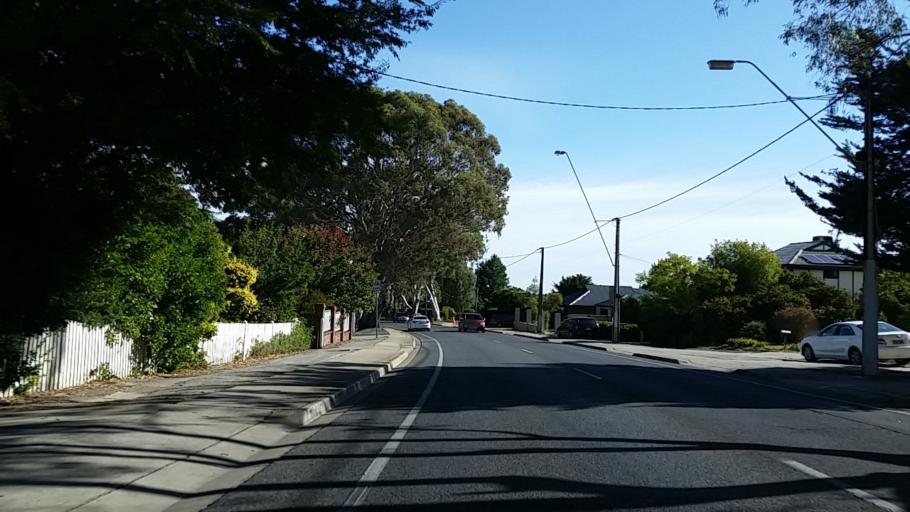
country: AU
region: South Australia
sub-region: Tea Tree Gully
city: Hope Valley
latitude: -34.8434
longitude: 138.7188
